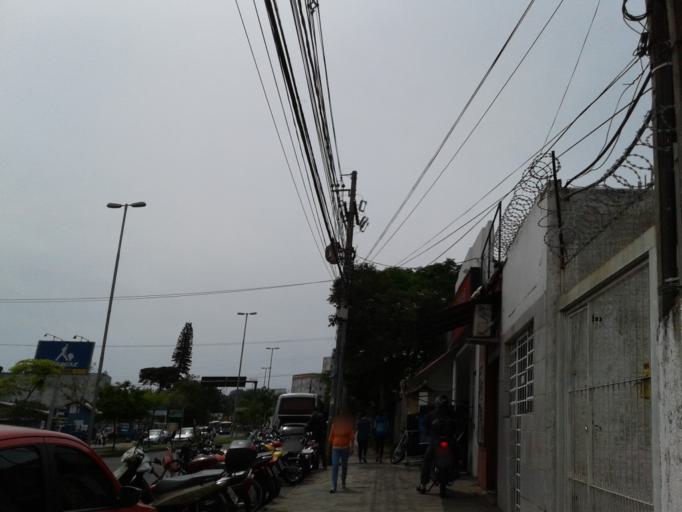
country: BR
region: Rio Grande do Sul
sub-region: Porto Alegre
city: Porto Alegre
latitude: -30.1381
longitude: -51.2209
